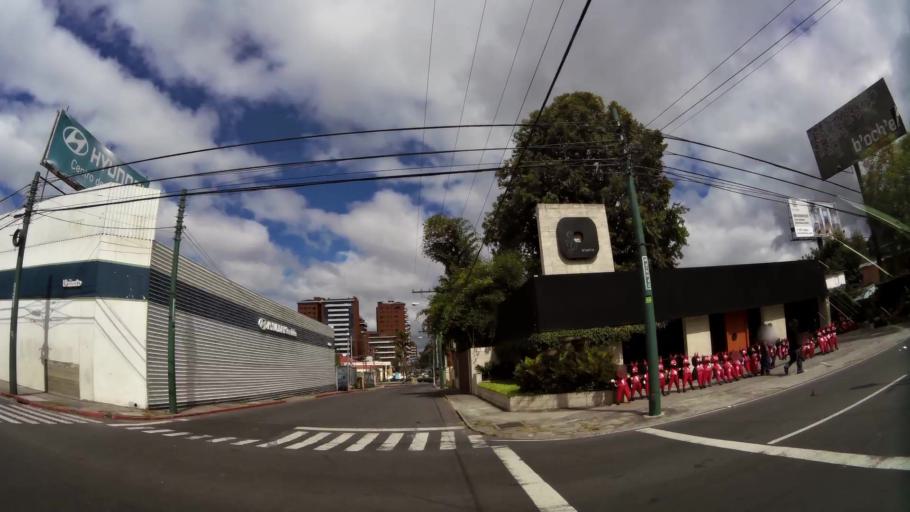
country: GT
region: Guatemala
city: Santa Catarina Pinula
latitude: 14.5903
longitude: -90.5107
